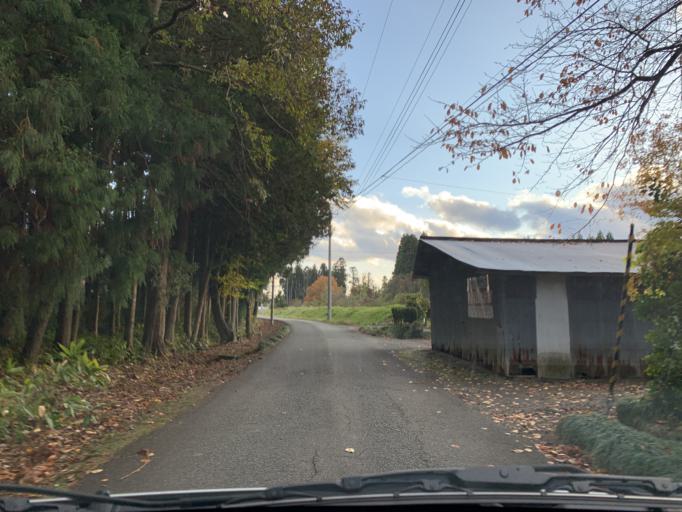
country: JP
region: Iwate
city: Mizusawa
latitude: 39.1081
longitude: 141.0394
